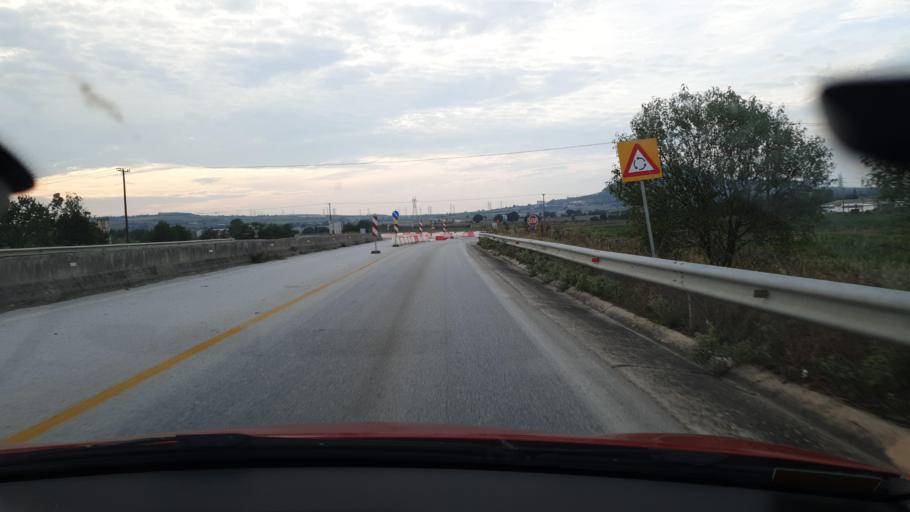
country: GR
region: Central Macedonia
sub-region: Nomos Thessalonikis
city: Assiros
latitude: 40.7857
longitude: 23.0104
